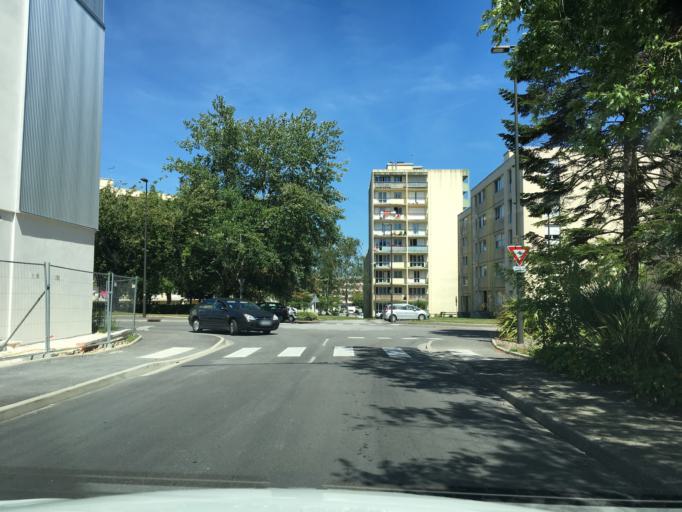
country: FR
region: Brittany
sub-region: Departement du Finistere
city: Quimper
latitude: 47.9853
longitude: -4.1272
